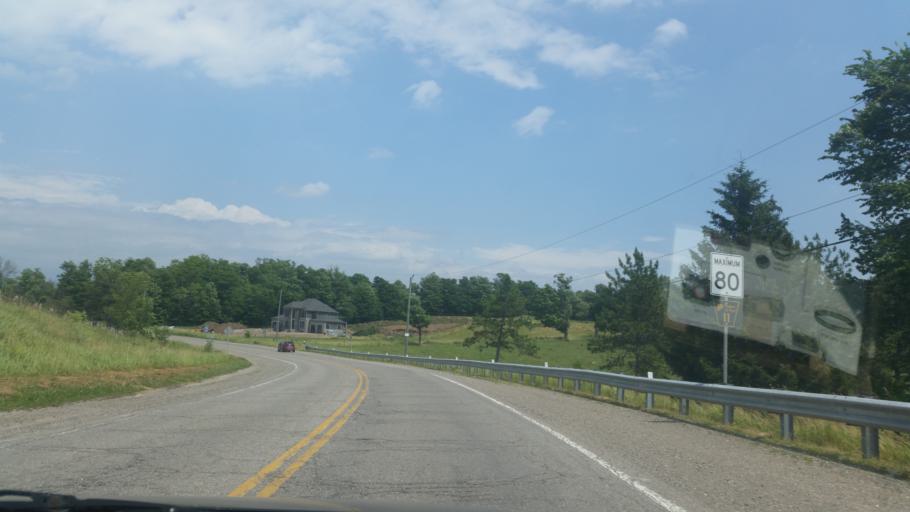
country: CA
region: Ontario
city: Orangeville
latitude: 43.7815
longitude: -80.0300
